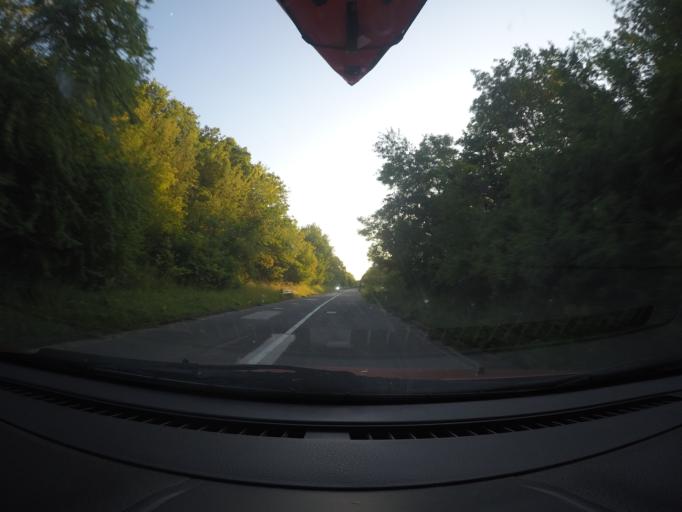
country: RO
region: Mehedinti
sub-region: Comuna Eselnita
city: Eselnita
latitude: 44.6726
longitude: 22.3868
